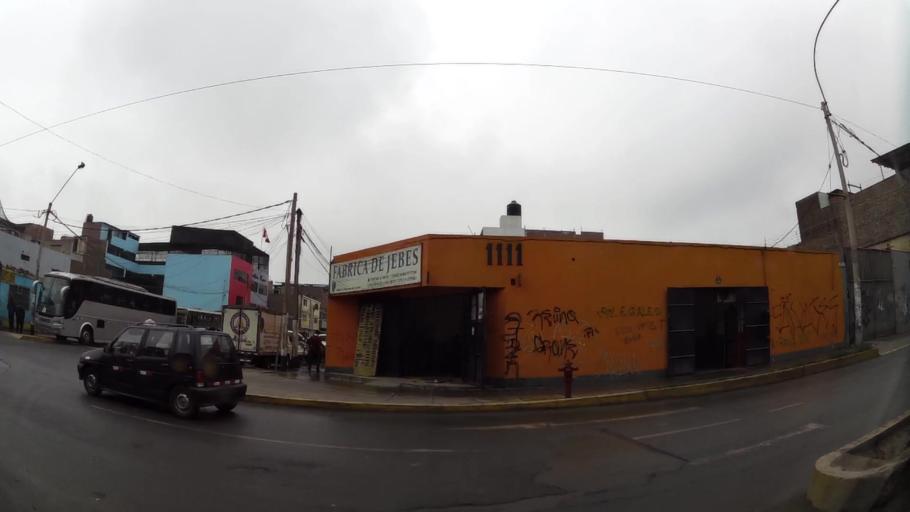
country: PE
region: Lima
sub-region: Lima
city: San Luis
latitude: -12.0690
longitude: -77.0188
